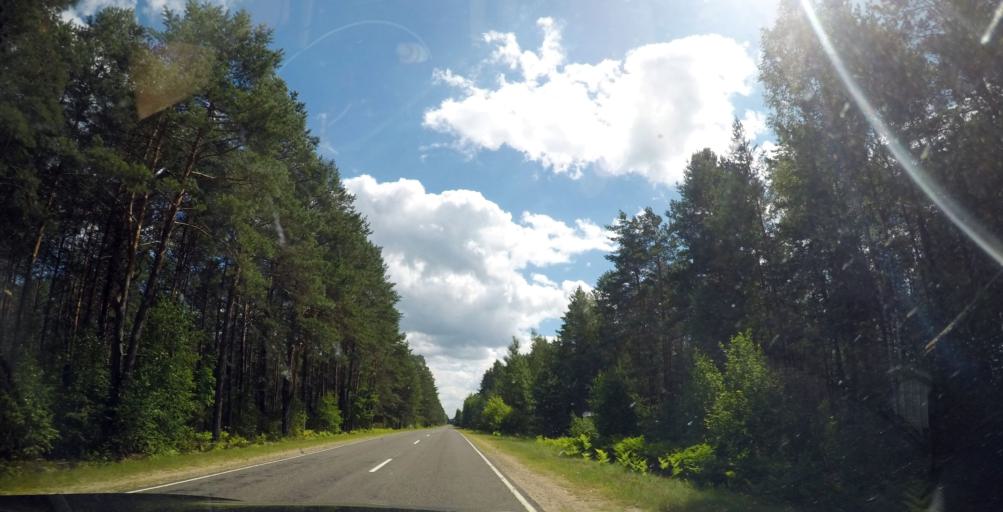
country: LT
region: Alytaus apskritis
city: Druskininkai
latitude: 53.8652
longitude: 24.1705
